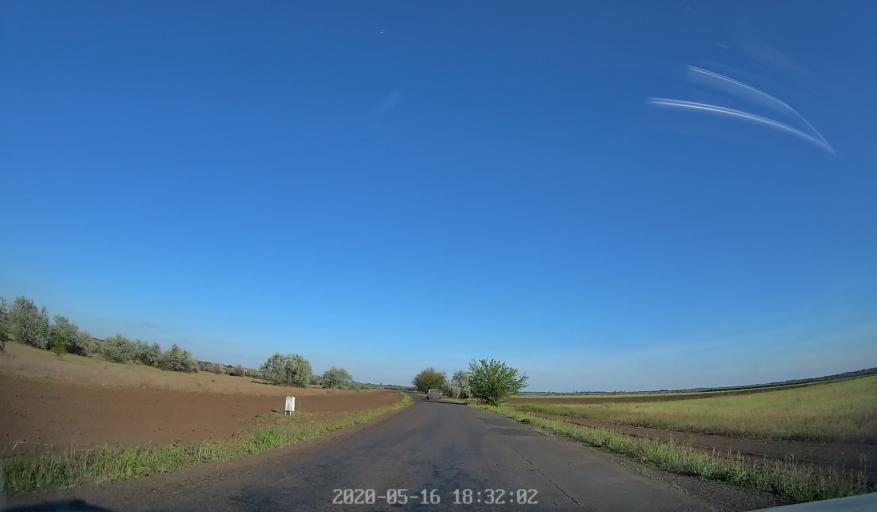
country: UA
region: Odessa
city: Lymanske
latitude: 46.5400
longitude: 30.0485
